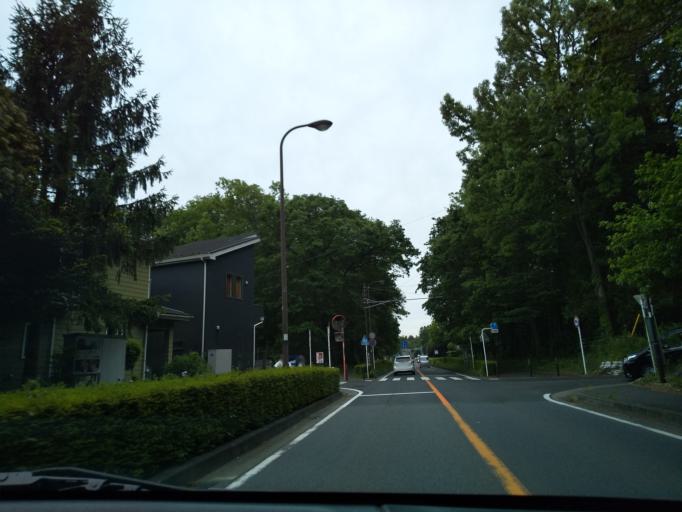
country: JP
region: Tokyo
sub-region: Machida-shi
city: Machida
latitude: 35.5407
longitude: 139.4125
